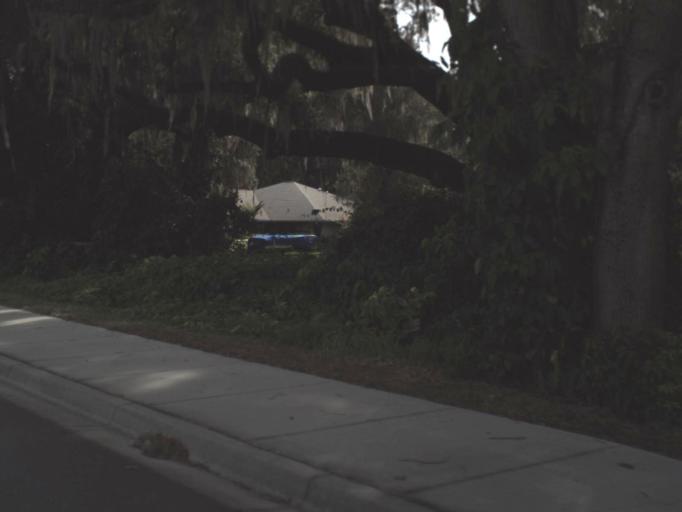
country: US
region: Florida
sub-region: Osceola County
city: Saint Cloud
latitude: 28.3434
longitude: -81.2285
